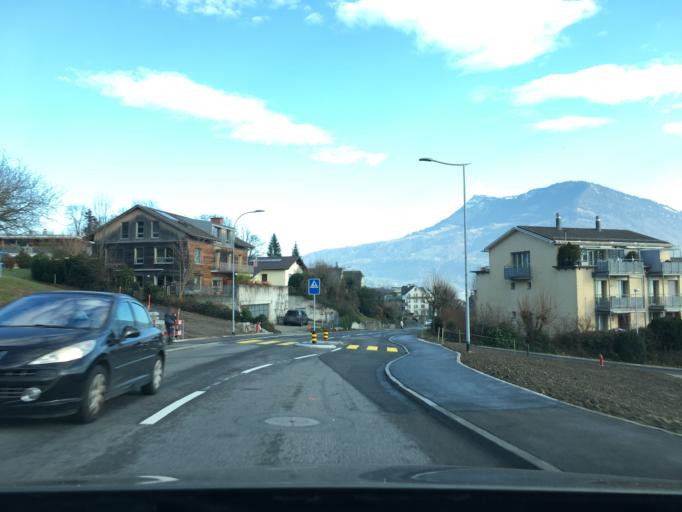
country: CH
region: Lucerne
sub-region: Lucerne-Land District
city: Meggen
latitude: 47.0511
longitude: 8.3790
